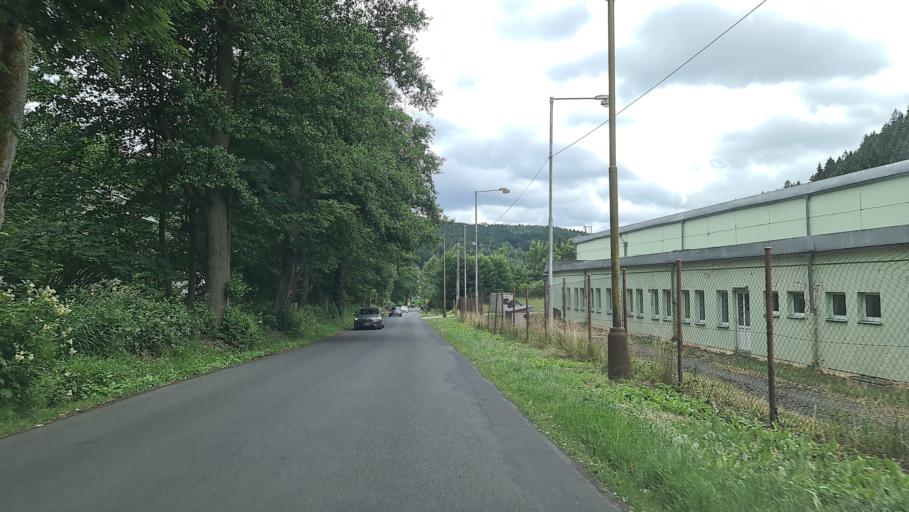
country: CZ
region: Karlovarsky
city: Kraslice
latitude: 50.3402
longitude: 12.5206
